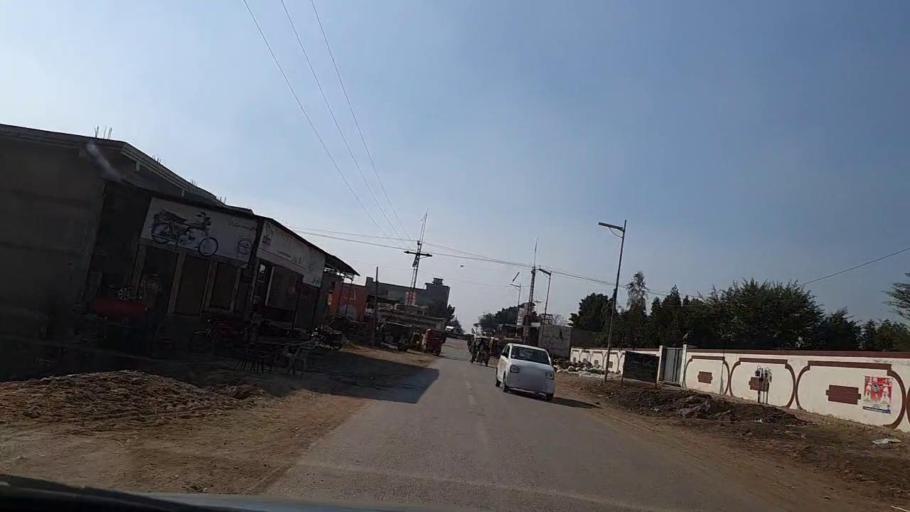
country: PK
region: Sindh
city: Sakrand
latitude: 26.1381
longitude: 68.2612
